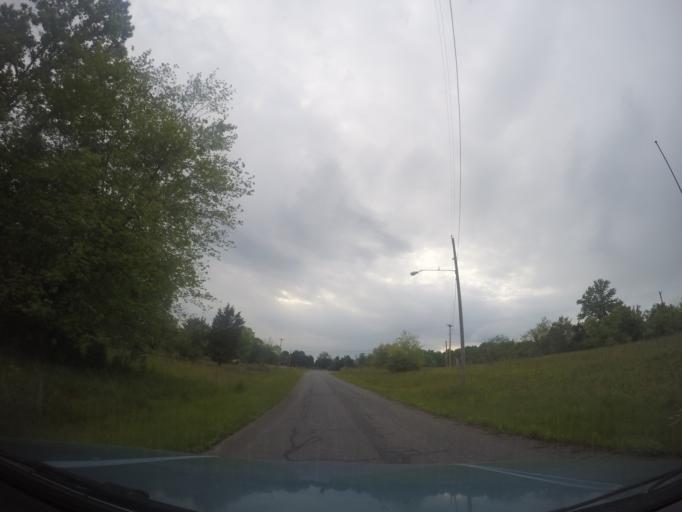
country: US
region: Virginia
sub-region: City of Lynchburg
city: Lynchburg
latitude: 37.3851
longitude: -79.1040
